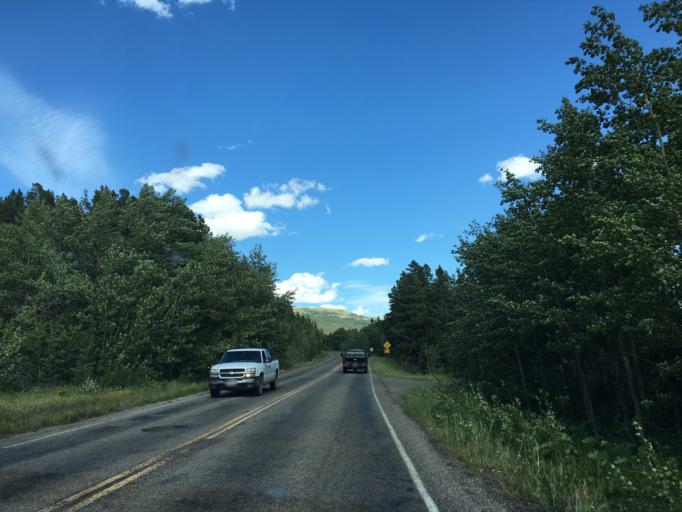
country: US
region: Montana
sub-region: Glacier County
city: South Browning
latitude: 48.5050
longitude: -113.3297
